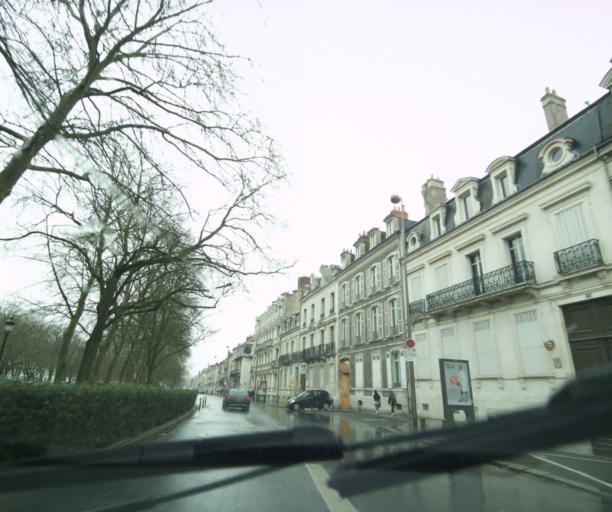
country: FR
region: Centre
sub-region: Departement du Loiret
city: Orleans
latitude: 47.9060
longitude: 1.9065
